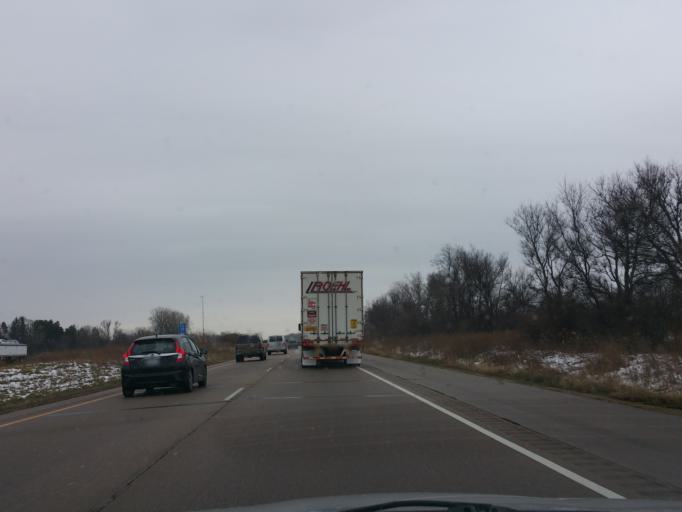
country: US
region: Wisconsin
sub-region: Rock County
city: Edgerton
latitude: 42.9019
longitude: -89.0810
